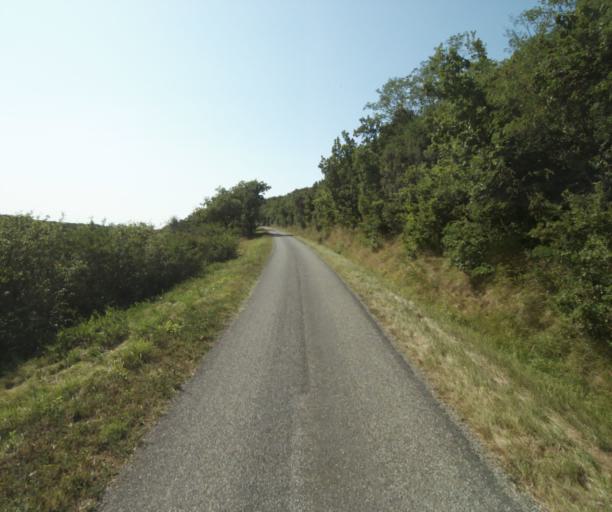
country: FR
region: Midi-Pyrenees
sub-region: Departement de la Haute-Garonne
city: Saint-Felix-Lauragais
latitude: 43.4391
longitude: 1.8350
